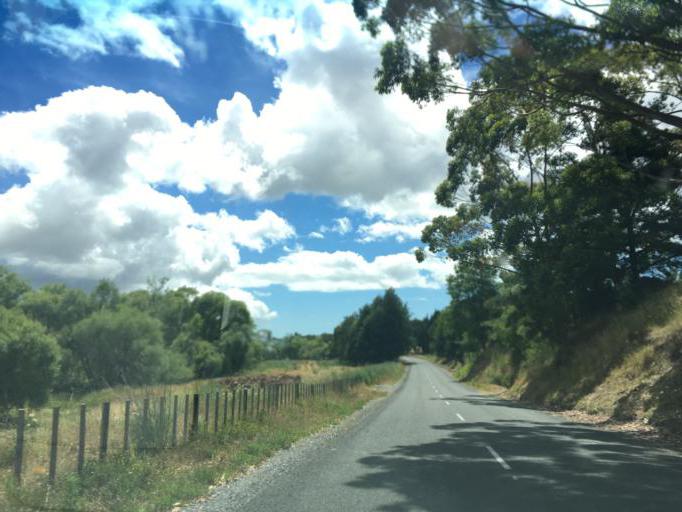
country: NZ
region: Hawke's Bay
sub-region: Hastings District
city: Hastings
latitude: -39.7535
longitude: 176.8703
